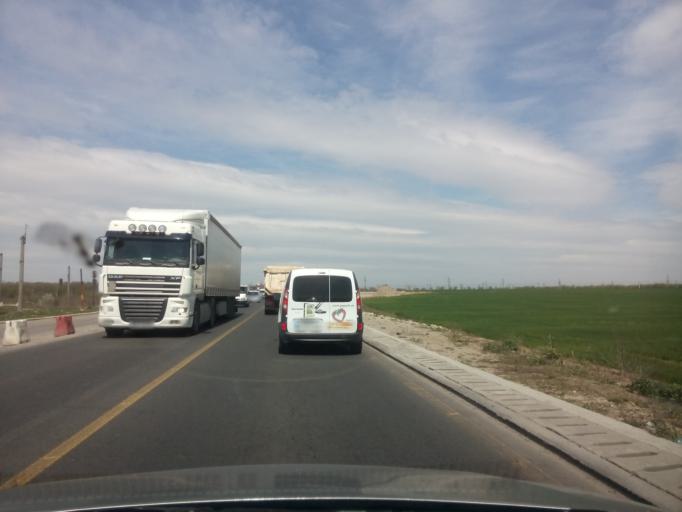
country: RO
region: Ilfov
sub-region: Comuna Pantelimon
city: Pantelimon
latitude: 44.4680
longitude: 26.2326
